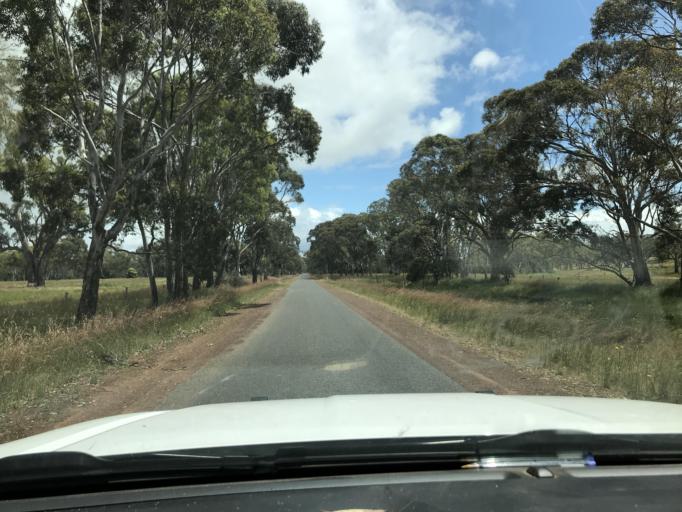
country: AU
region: Victoria
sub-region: Horsham
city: Horsham
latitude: -37.1219
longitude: 141.7000
